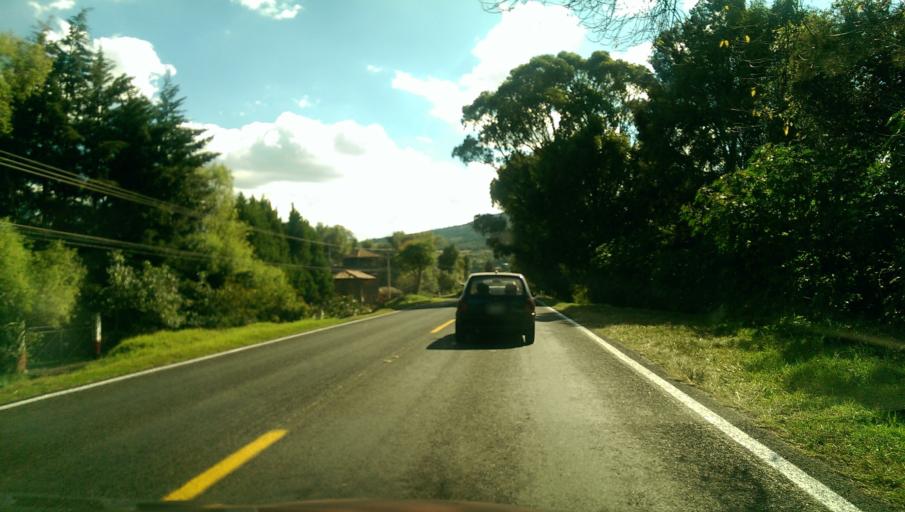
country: MX
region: Michoacan
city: Quiroga
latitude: 19.6461
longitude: -101.5338
